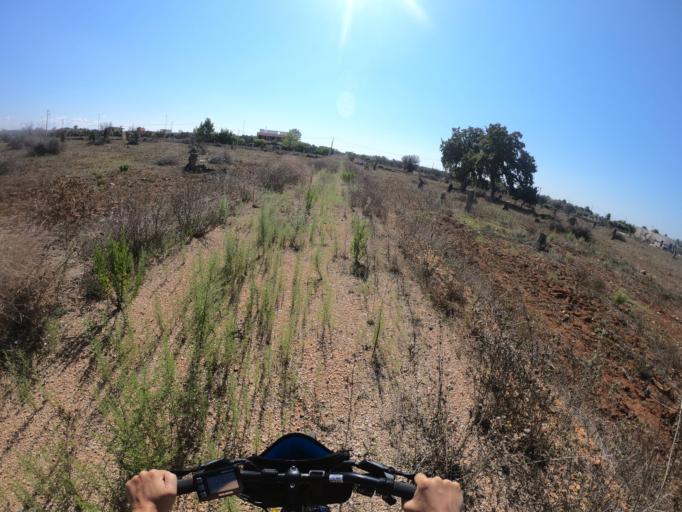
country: IT
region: Apulia
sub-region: Provincia di Lecce
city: Galatone
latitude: 40.1334
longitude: 18.0631
